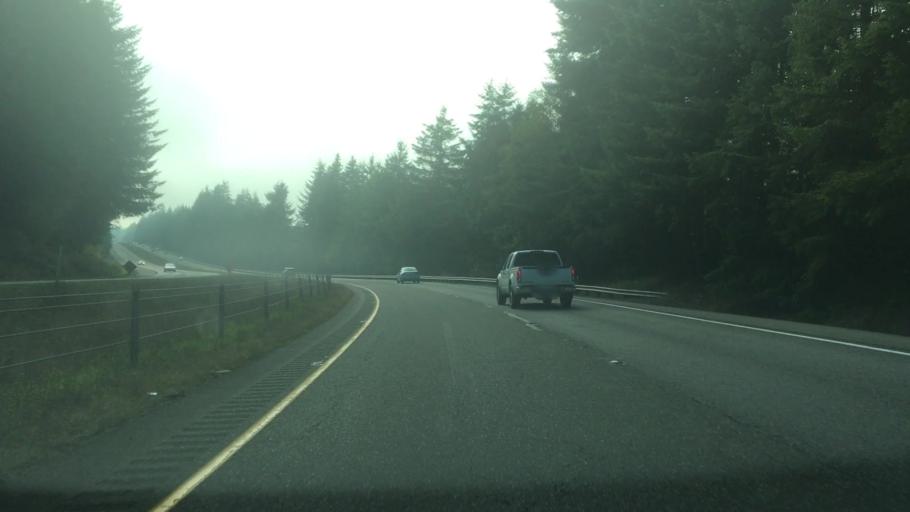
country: US
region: Washington
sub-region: Grays Harbor County
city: McCleary
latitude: 47.0379
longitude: -123.3325
